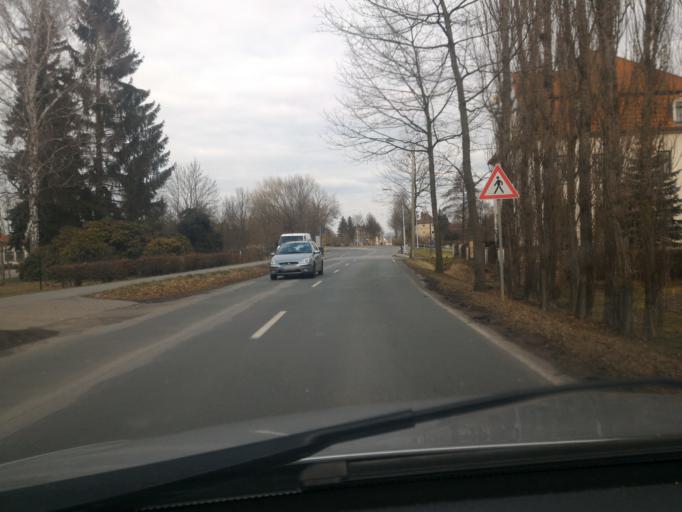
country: DE
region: Saxony
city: Zittau
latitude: 50.8760
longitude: 14.8109
